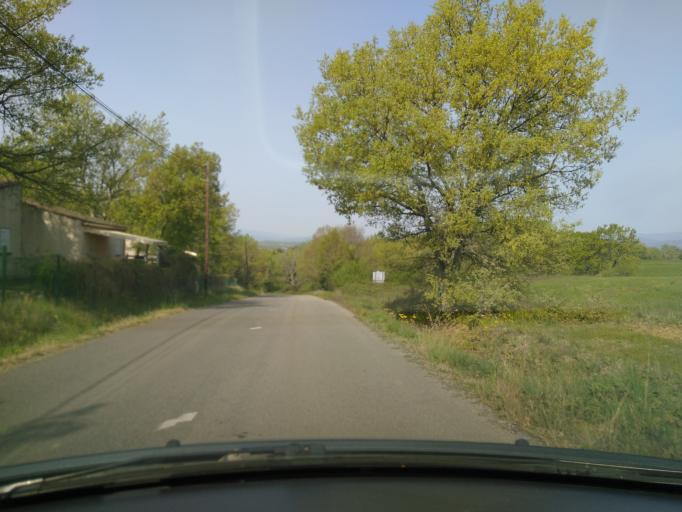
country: FR
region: Rhone-Alpes
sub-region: Departement de l'Ardeche
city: Ruoms
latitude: 44.4478
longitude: 4.3688
